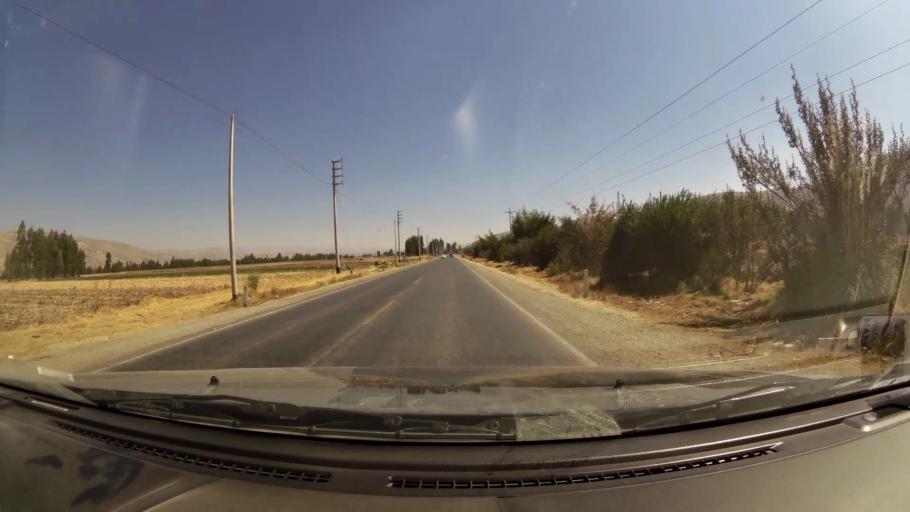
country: PE
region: Junin
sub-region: Provincia de Jauja
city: Huamali
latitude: -11.8193
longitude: -75.4167
